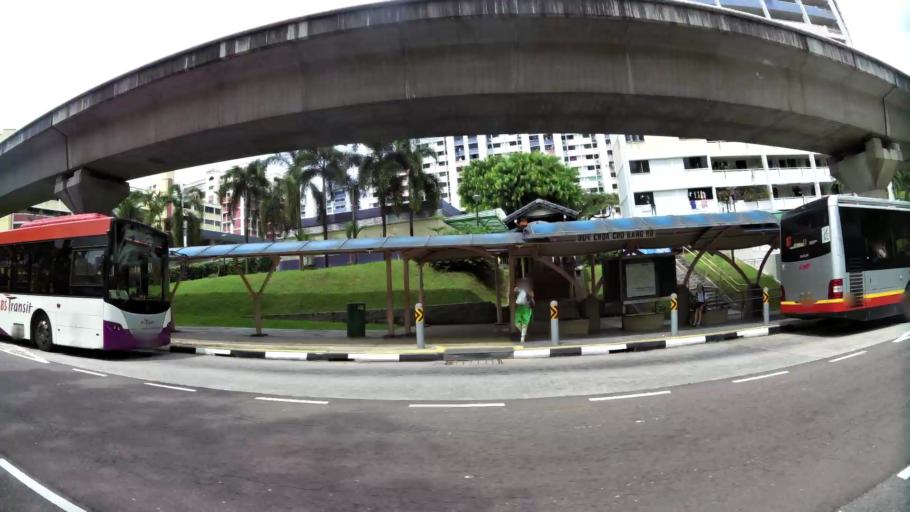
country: MY
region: Johor
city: Johor Bahru
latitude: 1.3771
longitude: 103.7554
